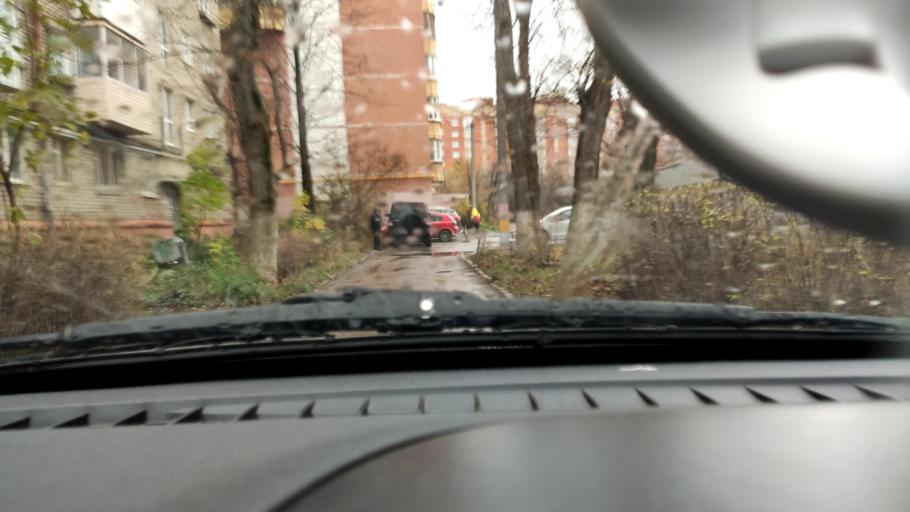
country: RU
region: Perm
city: Perm
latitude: 57.9994
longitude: 56.2852
